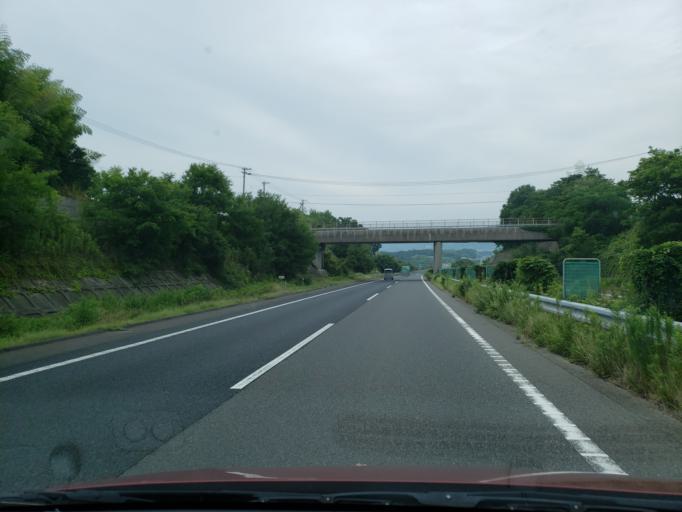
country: JP
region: Hyogo
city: Sumoto
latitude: 34.4340
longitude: 134.8703
